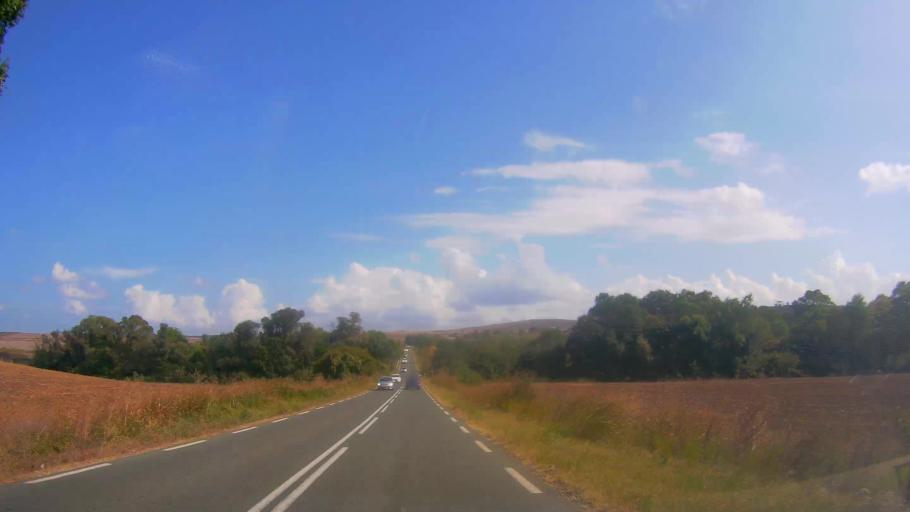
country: BG
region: Burgas
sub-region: Obshtina Burgas
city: Burgas
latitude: 42.4764
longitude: 27.3562
